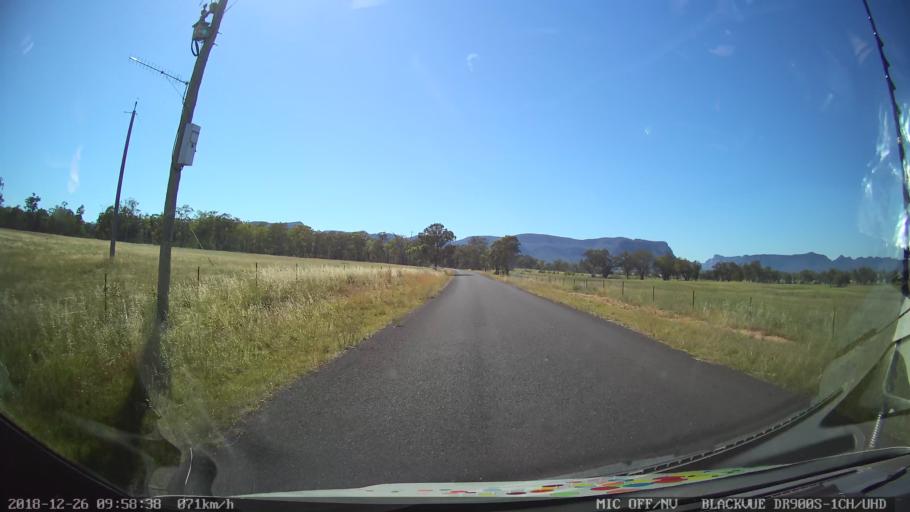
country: AU
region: New South Wales
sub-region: Mid-Western Regional
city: Kandos
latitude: -33.0397
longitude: 150.2068
